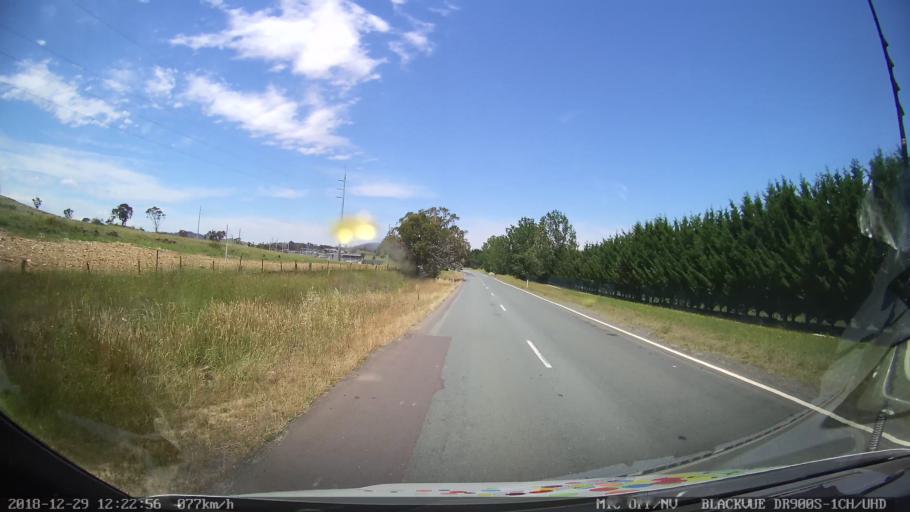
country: AU
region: New South Wales
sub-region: Queanbeyan
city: Queanbeyan
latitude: -35.4304
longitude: 149.2185
